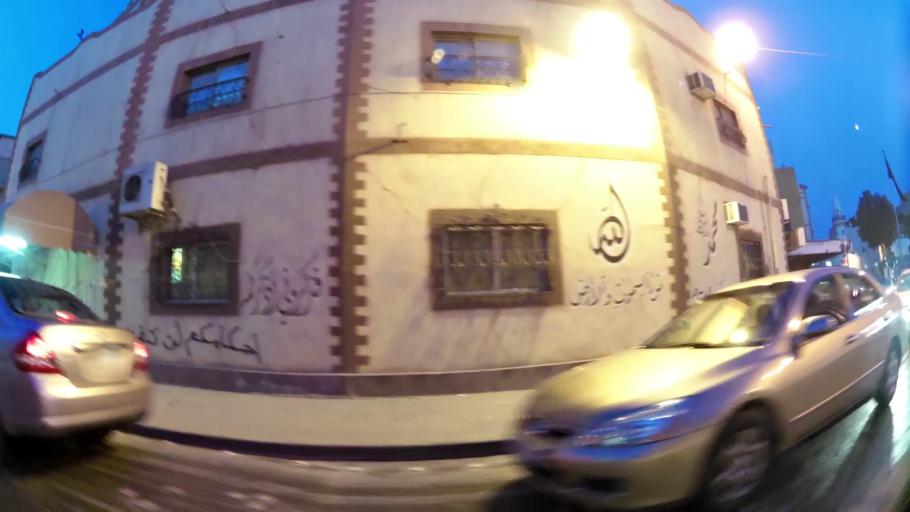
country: BH
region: Manama
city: Jidd Hafs
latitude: 26.2053
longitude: 50.5516
